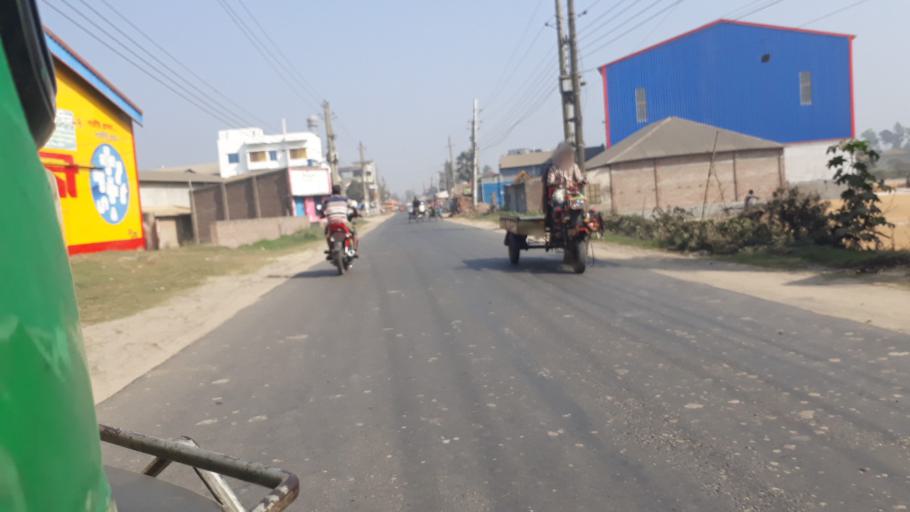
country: BD
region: Khulna
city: Kushtia
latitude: 23.8654
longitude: 89.0549
